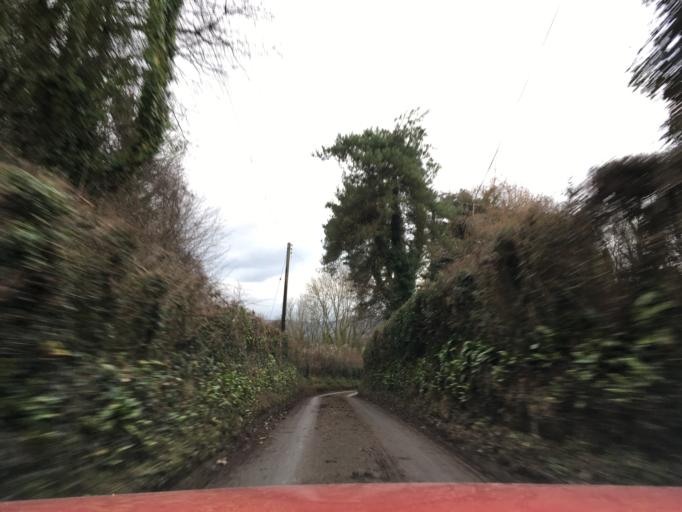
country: GB
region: Wales
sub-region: Monmouthshire
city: Rogiet
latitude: 51.6012
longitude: -2.7808
